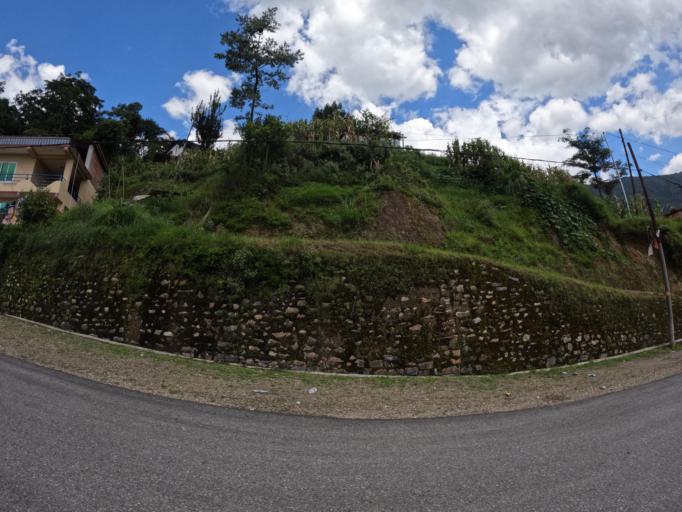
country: NP
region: Central Region
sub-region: Bagmati Zone
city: Kathmandu
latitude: 27.8018
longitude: 85.3256
